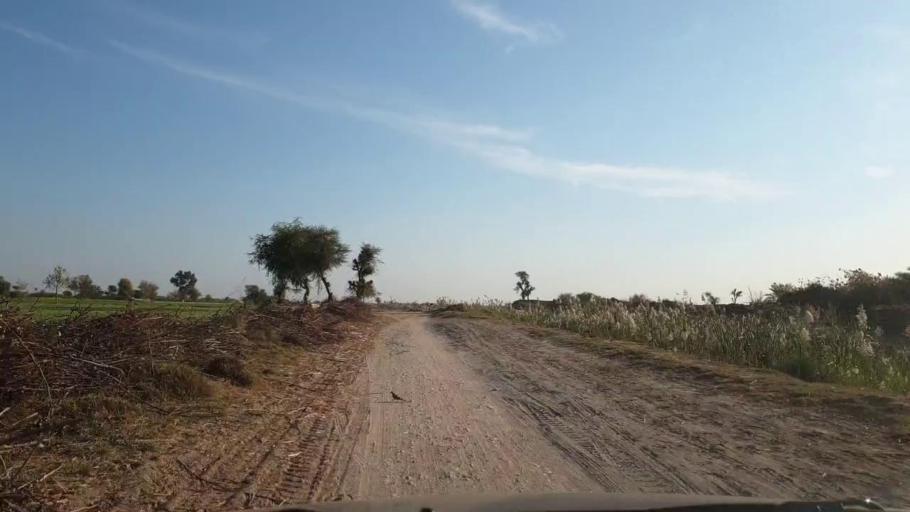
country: PK
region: Sindh
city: Khadro
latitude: 26.2154
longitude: 68.7416
